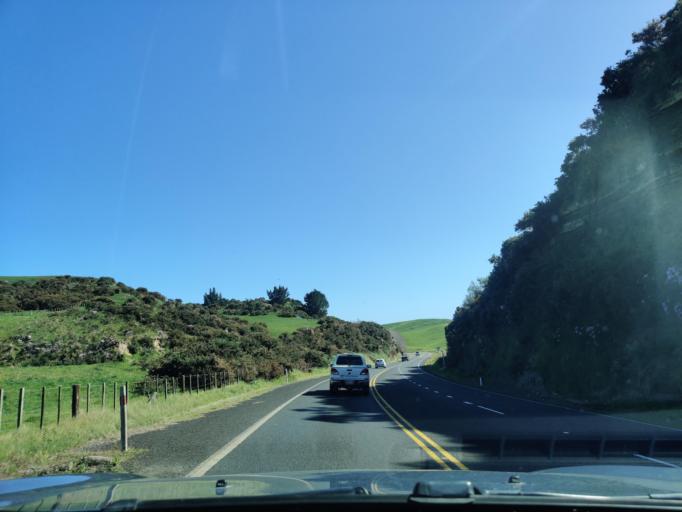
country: NZ
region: Manawatu-Wanganui
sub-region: Wanganui District
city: Wanganui
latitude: -40.0225
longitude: 175.1790
